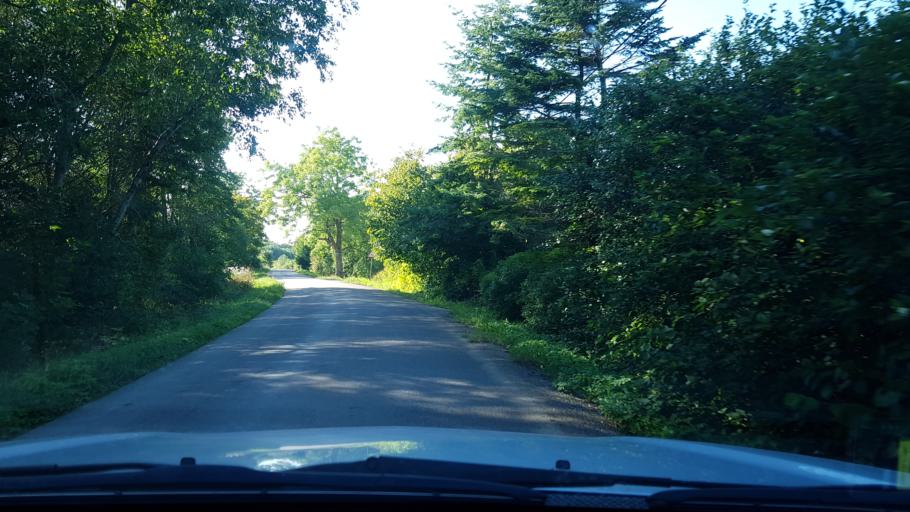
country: EE
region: Ida-Virumaa
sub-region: Narva-Joesuu linn
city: Narva-Joesuu
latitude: 59.4087
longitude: 27.9866
